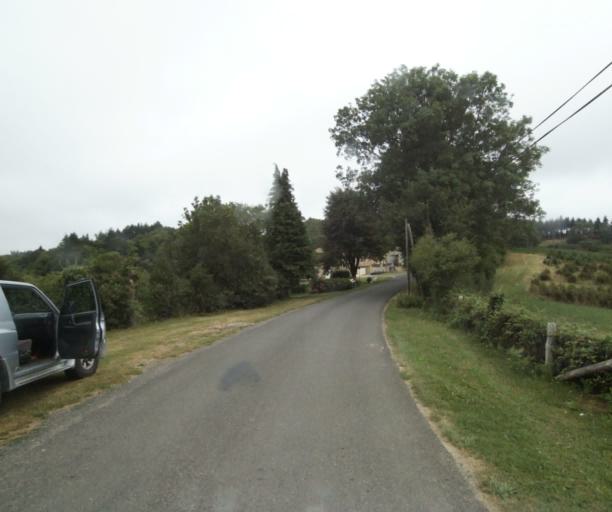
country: FR
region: Midi-Pyrenees
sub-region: Departement du Tarn
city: Soreze
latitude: 43.4100
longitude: 2.0550
